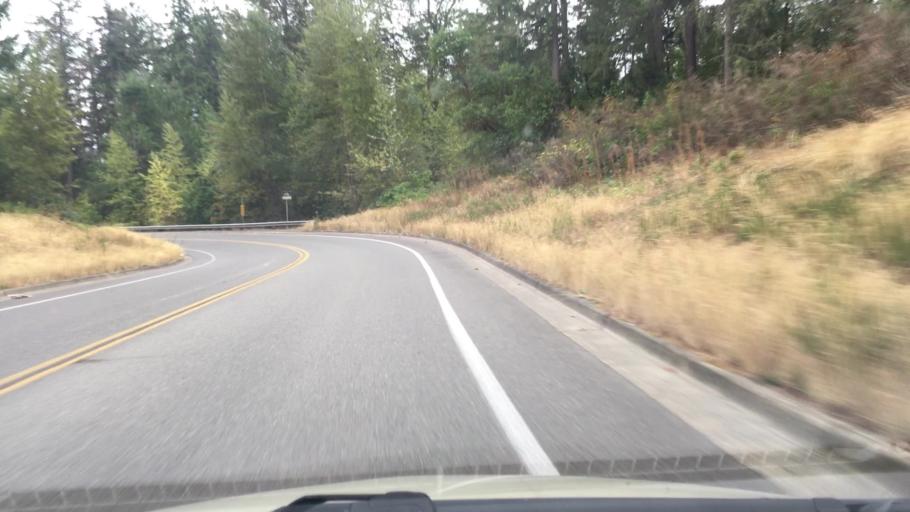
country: US
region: Washington
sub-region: Pierce County
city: Fort Lewis
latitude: 47.1088
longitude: -122.5902
